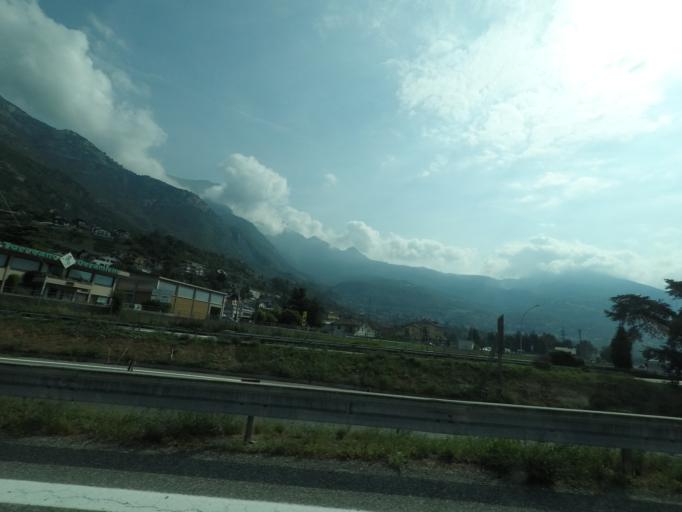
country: IT
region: Aosta Valley
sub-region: Valle d'Aosta
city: Chatillon
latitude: 45.7488
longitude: 7.6213
